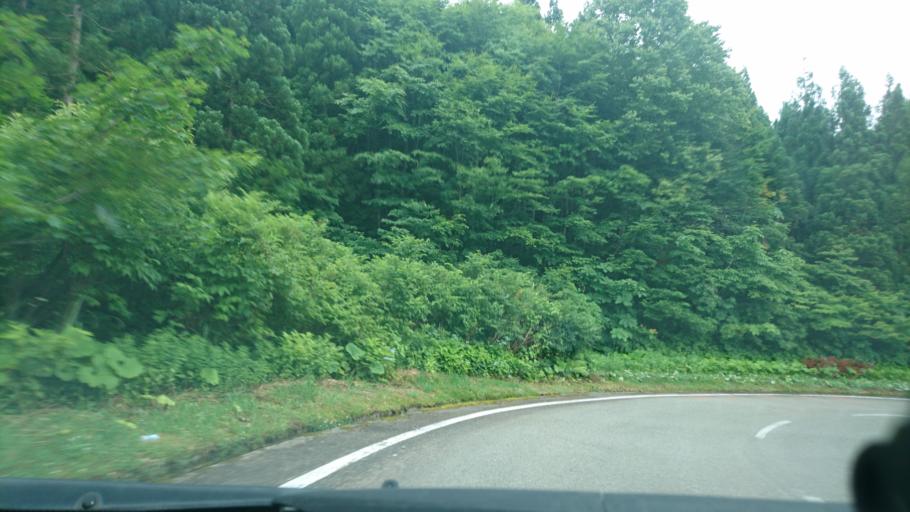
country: JP
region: Akita
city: Yuzawa
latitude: 39.1562
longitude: 140.7486
